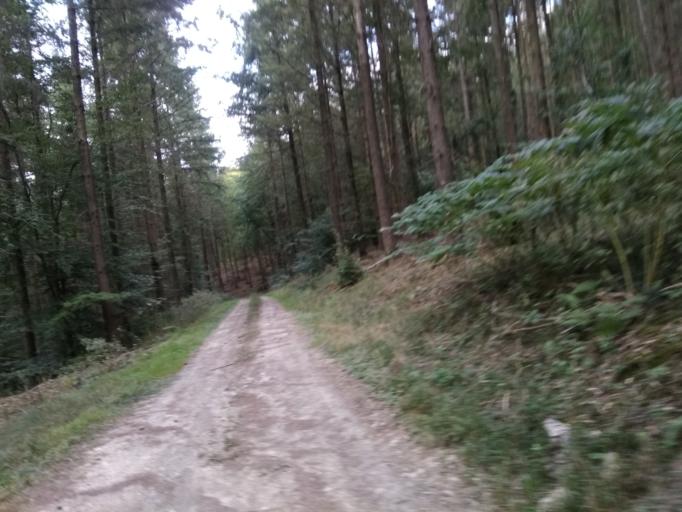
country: DE
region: Baden-Wuerttemberg
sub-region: Karlsruhe Region
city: Obrigheim
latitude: 49.3750
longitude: 9.1067
